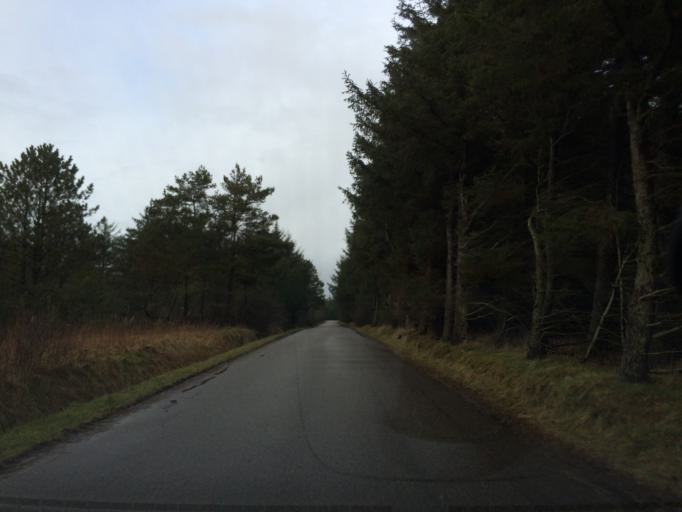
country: DK
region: Central Jutland
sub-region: Holstebro Kommune
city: Ulfborg
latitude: 56.2746
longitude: 8.1587
